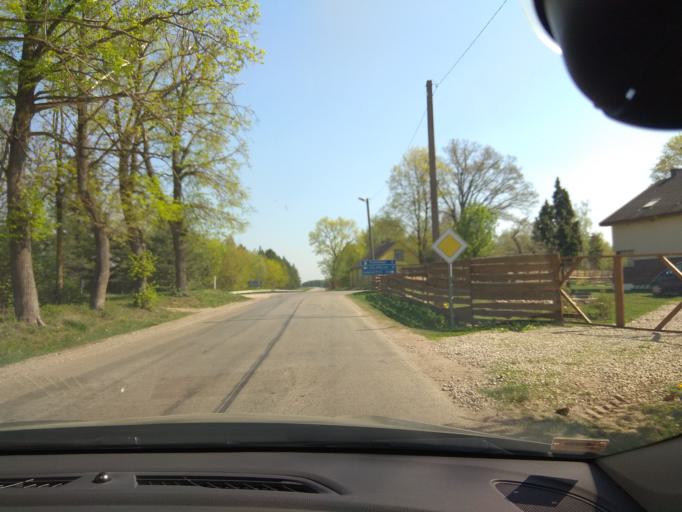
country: LT
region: Panevezys
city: Pasvalys
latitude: 55.9368
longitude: 24.2395
